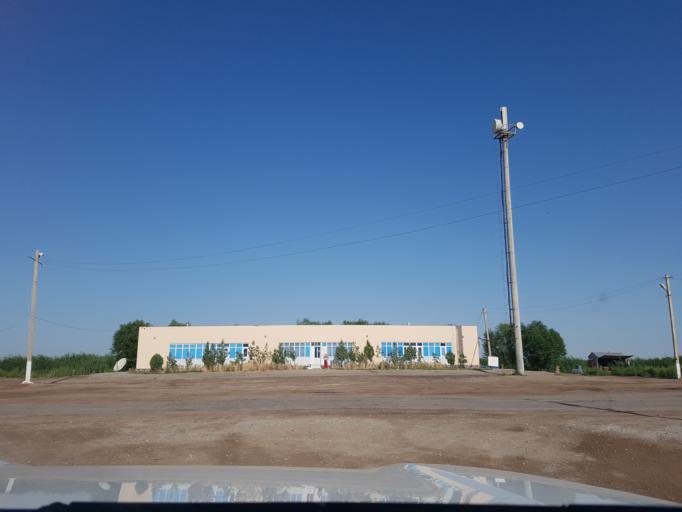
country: TM
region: Dasoguz
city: Koeneuergench
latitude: 41.8791
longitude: 58.7067
